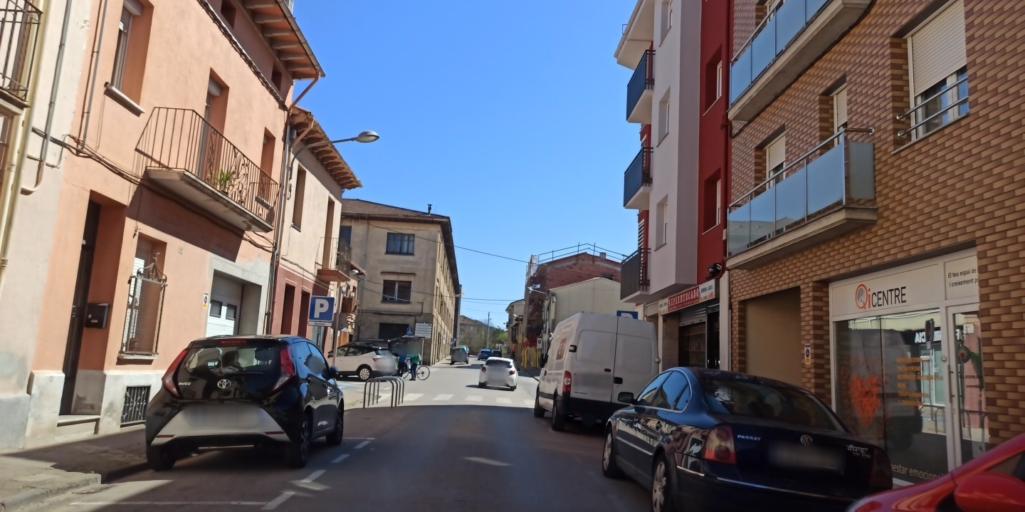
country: ES
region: Catalonia
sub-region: Provincia de Girona
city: MeteOlot
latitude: 42.1848
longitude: 2.4831
